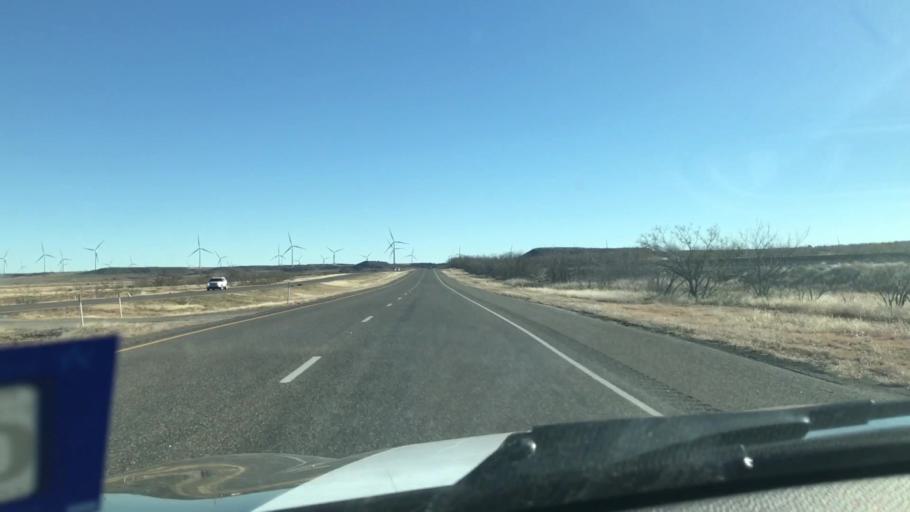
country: US
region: Texas
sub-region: Scurry County
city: Snyder
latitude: 32.9283
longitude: -101.0676
